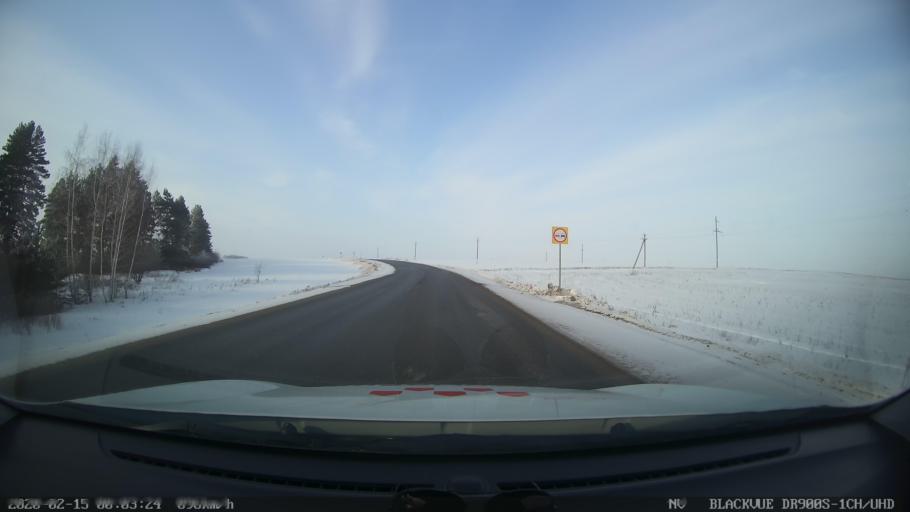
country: RU
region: Tatarstan
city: Kuybyshevskiy Zaton
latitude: 55.3714
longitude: 48.9980
